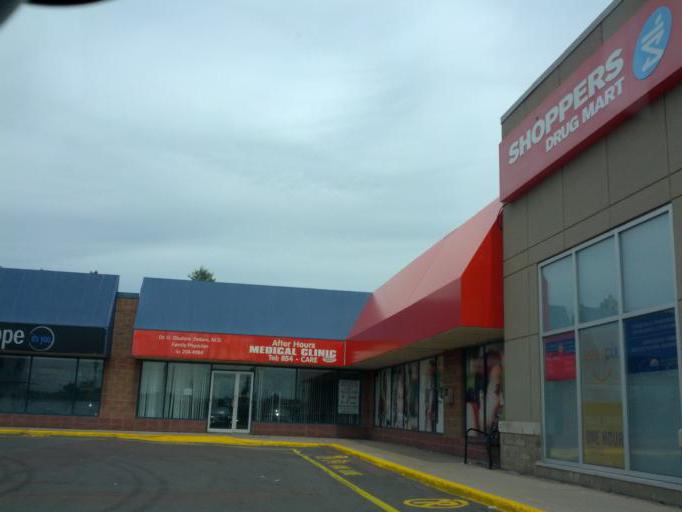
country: CA
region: New Brunswick
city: Moncton
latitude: 46.1172
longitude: -64.8394
